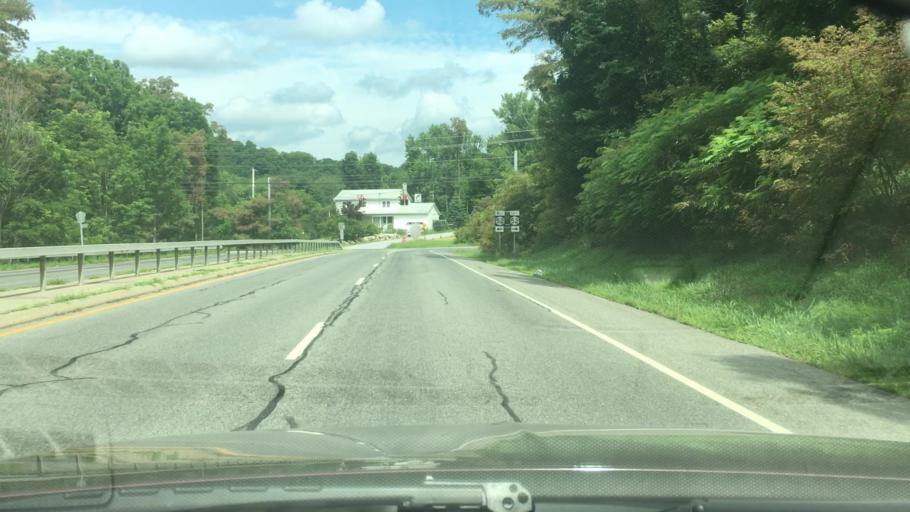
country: US
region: New York
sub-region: Dutchess County
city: Brinckerhoff
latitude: 41.5466
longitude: -73.8180
